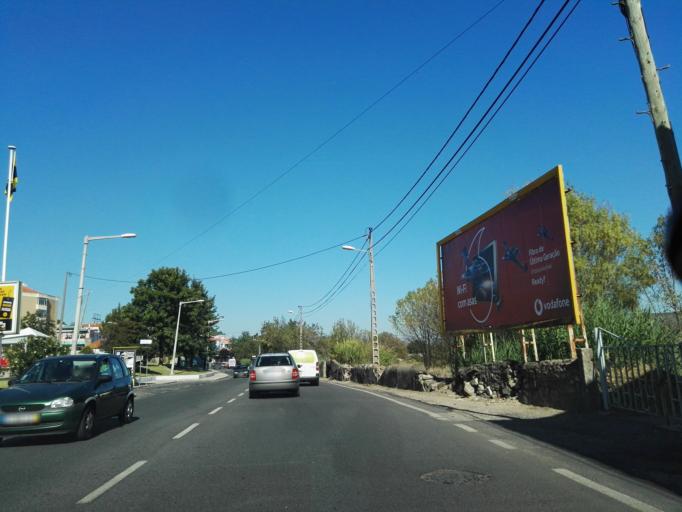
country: PT
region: Lisbon
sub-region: Odivelas
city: Povoa de Santo Adriao
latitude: 38.8128
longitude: -9.1559
